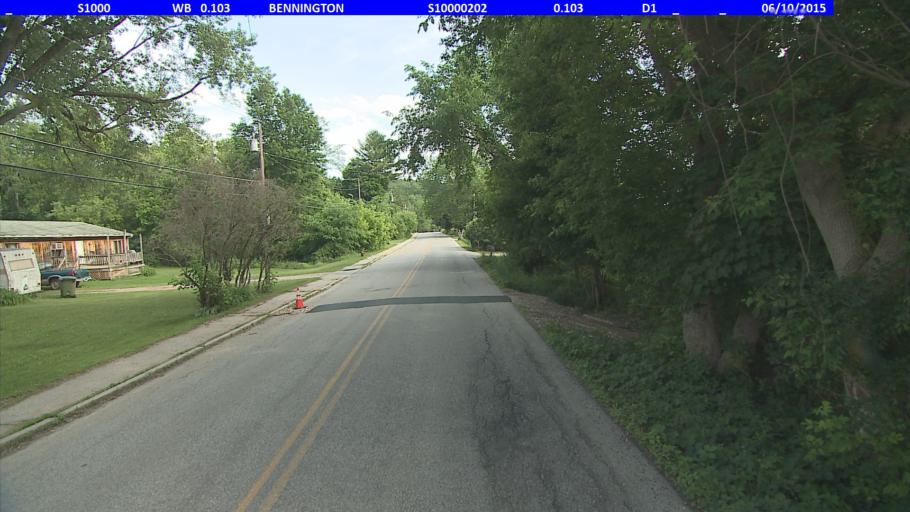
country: US
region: Vermont
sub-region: Bennington County
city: Bennington
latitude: 42.8705
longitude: -73.1767
